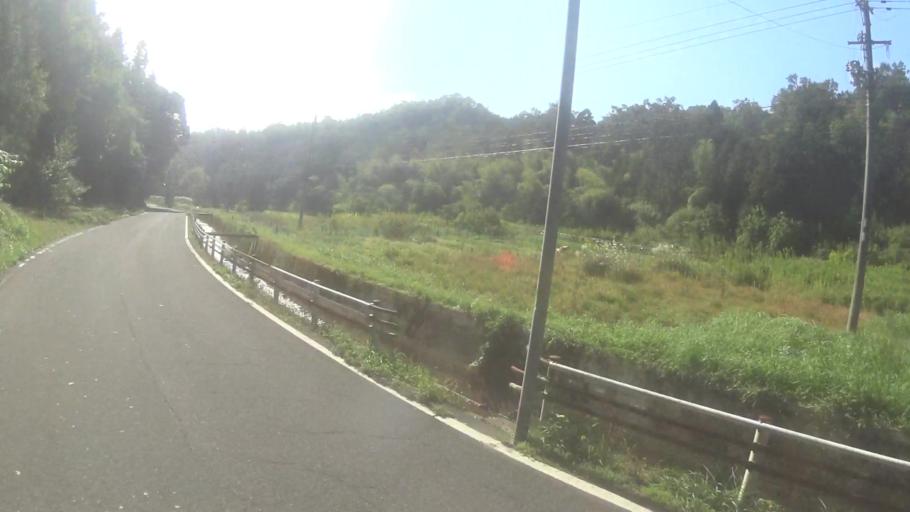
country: JP
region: Kyoto
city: Miyazu
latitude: 35.6857
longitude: 135.1121
